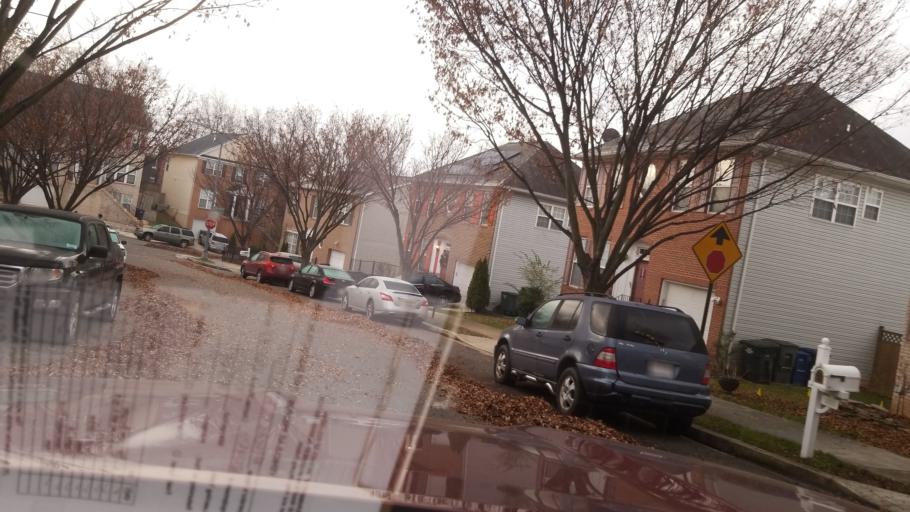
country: US
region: Maryland
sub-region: Prince George's County
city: Glassmanor
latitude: 38.8409
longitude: -76.9963
